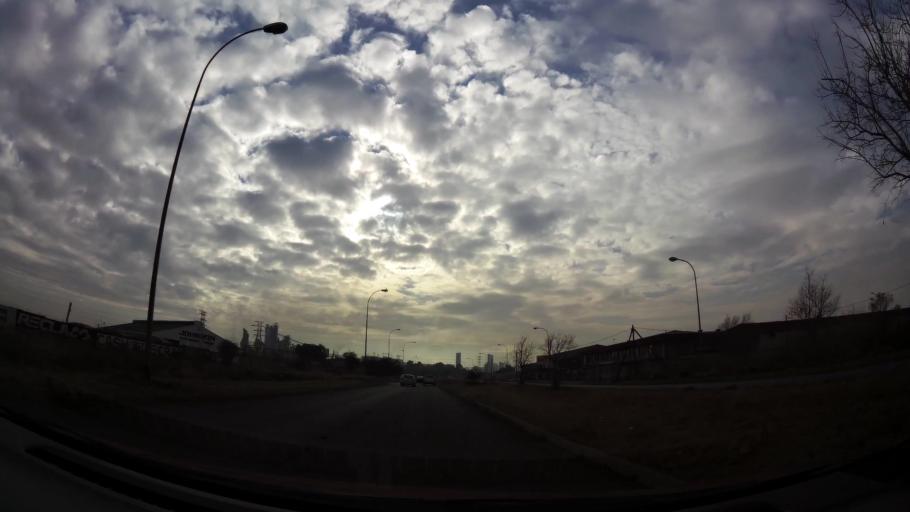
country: ZA
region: Gauteng
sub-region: Sedibeng District Municipality
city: Vanderbijlpark
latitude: -26.6760
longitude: 27.7955
